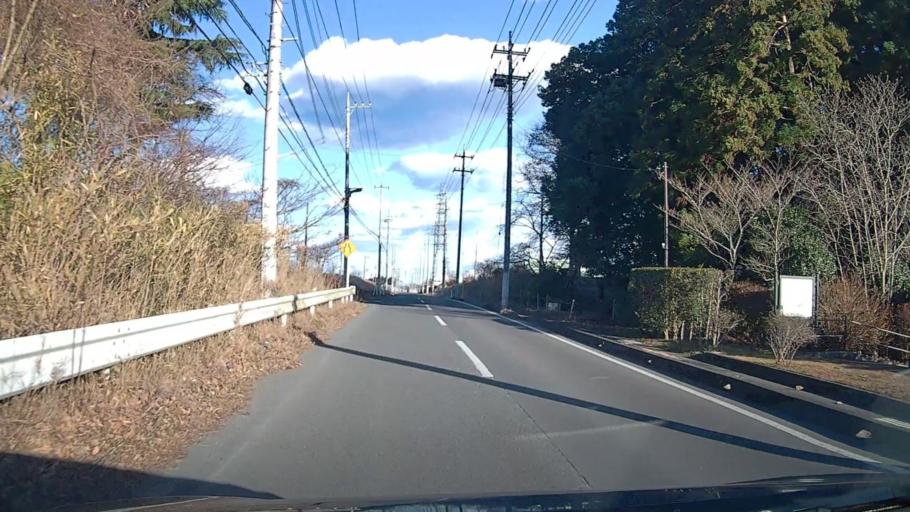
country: JP
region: Ibaraki
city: Mito-shi
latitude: 36.4405
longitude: 140.4445
